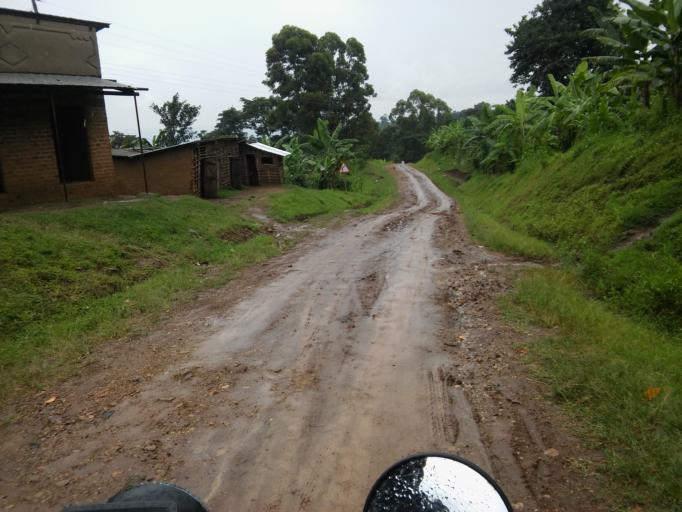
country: UG
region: Eastern Region
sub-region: Bududa District
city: Bududa
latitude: 1.0065
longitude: 34.2387
